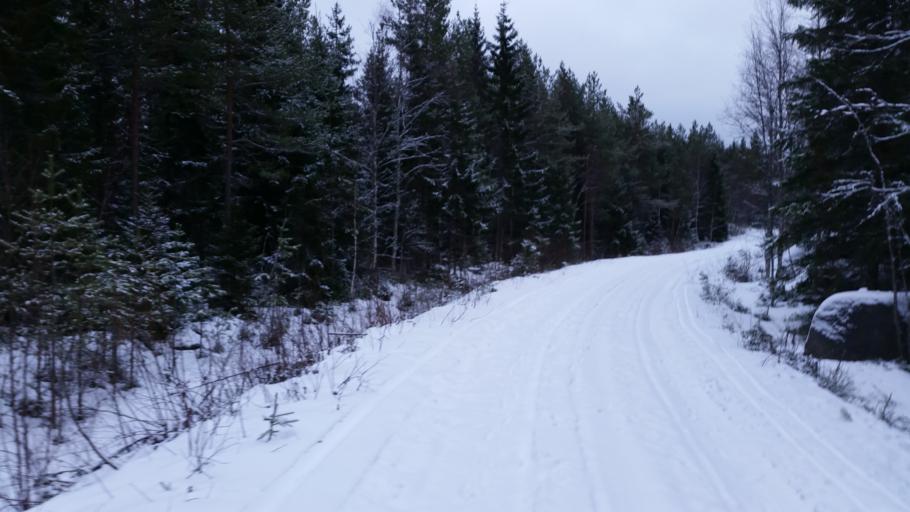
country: SE
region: Vaesterbotten
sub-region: Umea Kommun
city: Saevar
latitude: 63.9177
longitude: 20.7808
